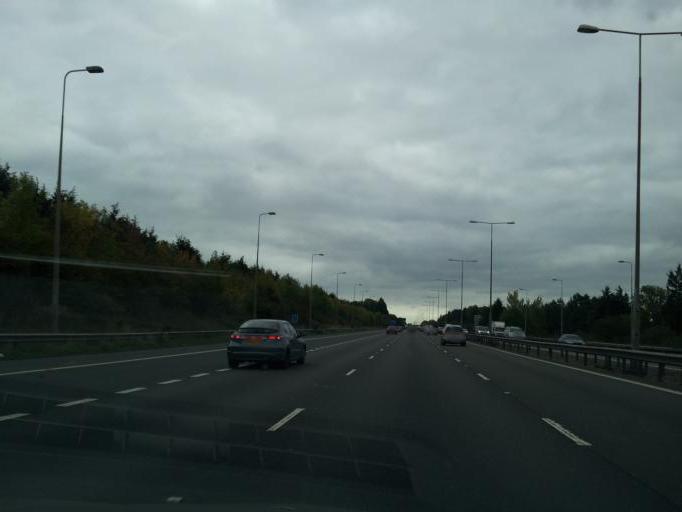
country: GB
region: England
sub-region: Northamptonshire
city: Roade
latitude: 52.1826
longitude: -0.8894
